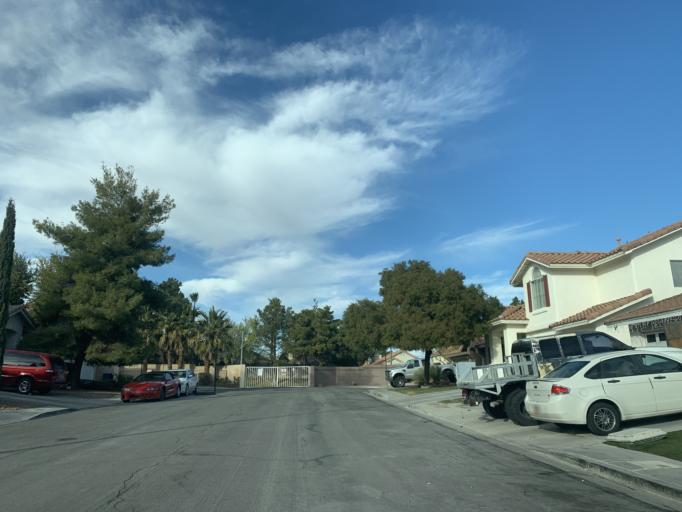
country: US
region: Nevada
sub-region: Clark County
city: Summerlin South
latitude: 36.1293
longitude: -115.3046
